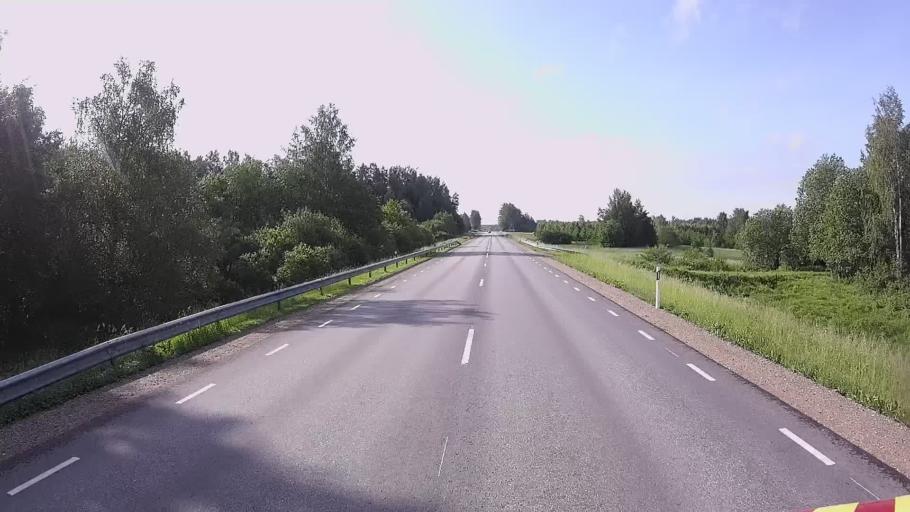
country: EE
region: Viljandimaa
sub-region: Viljandi linn
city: Viljandi
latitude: 58.3496
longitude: 25.5625
